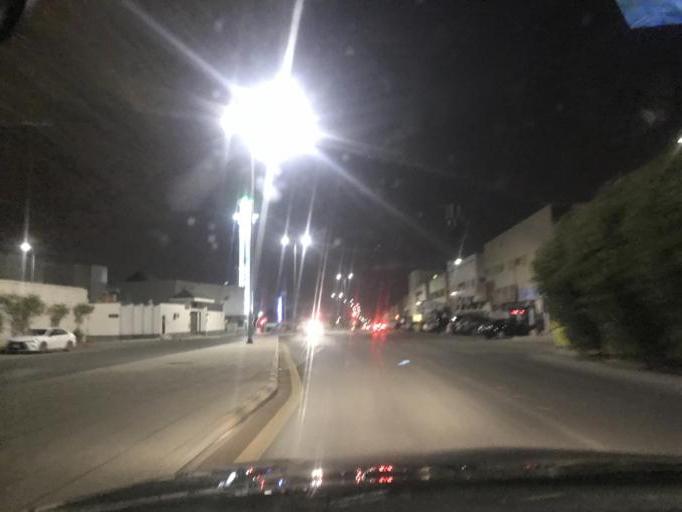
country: SA
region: Ar Riyad
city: Riyadh
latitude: 24.7112
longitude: 46.7776
